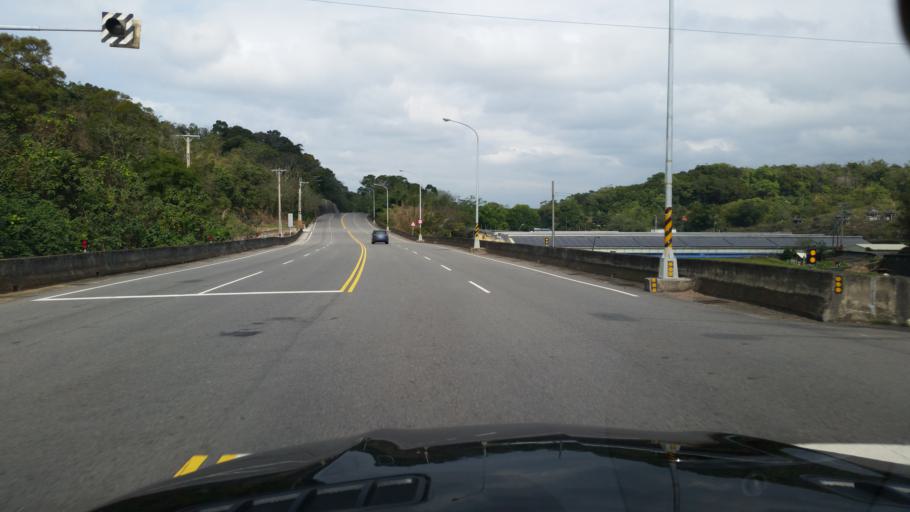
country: TW
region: Taiwan
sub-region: Miaoli
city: Miaoli
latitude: 24.6453
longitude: 120.8609
